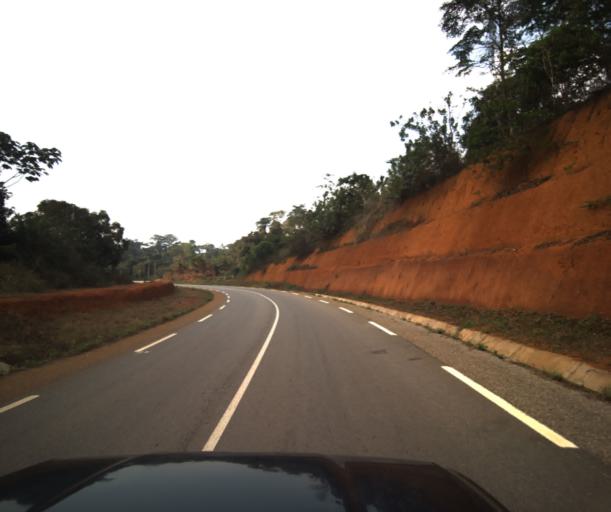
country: CM
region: Centre
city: Mbankomo
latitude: 3.6629
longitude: 11.3430
